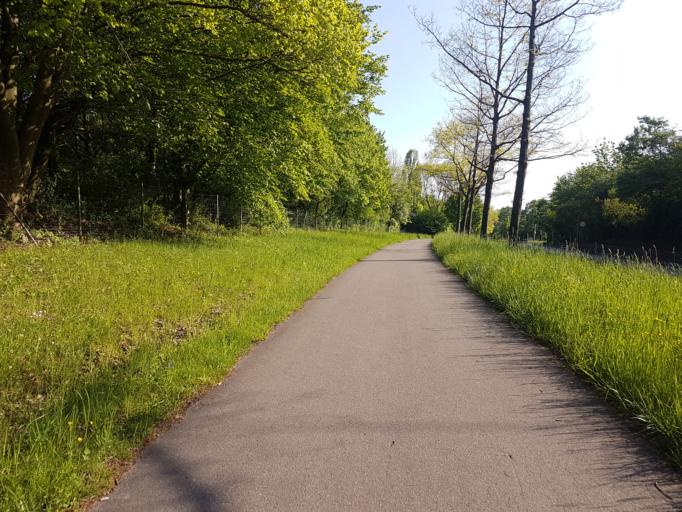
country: DE
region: Baden-Wuerttemberg
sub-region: Regierungsbezirk Stuttgart
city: Kornwestheim
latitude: 48.8395
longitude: 9.1766
